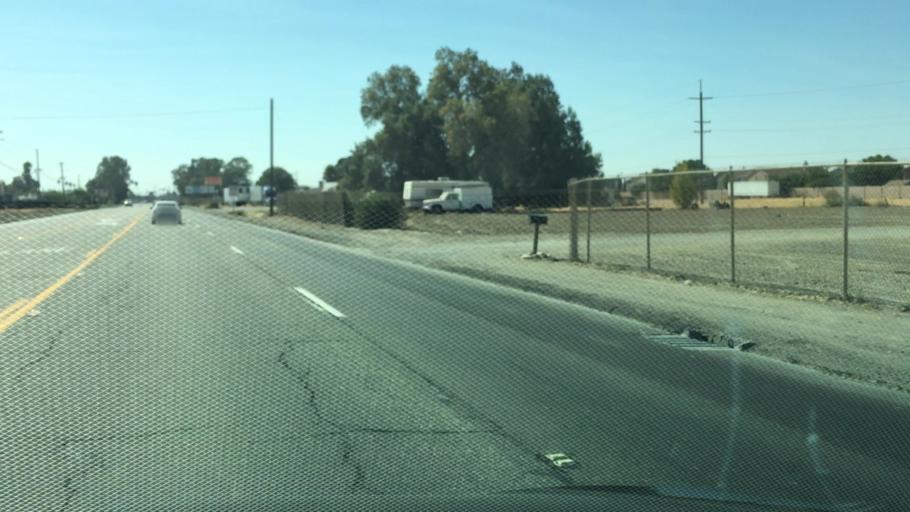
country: US
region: California
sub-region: Merced County
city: Los Banos
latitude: 37.0566
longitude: -120.8105
